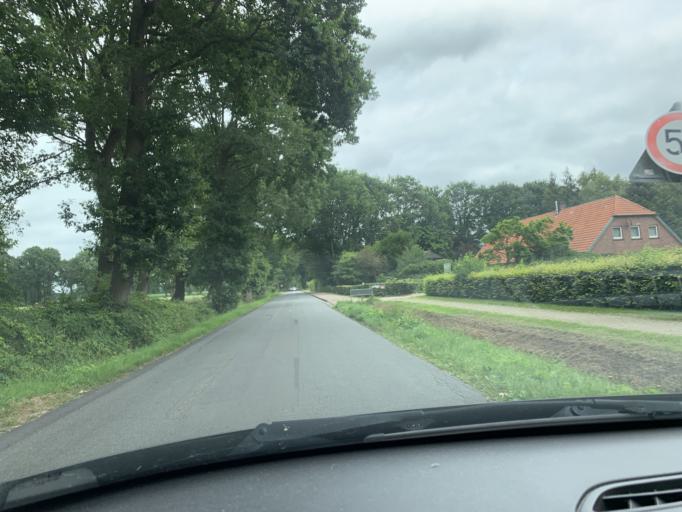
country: DE
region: Lower Saxony
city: Wiefelstede
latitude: 53.1840
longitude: 8.1382
